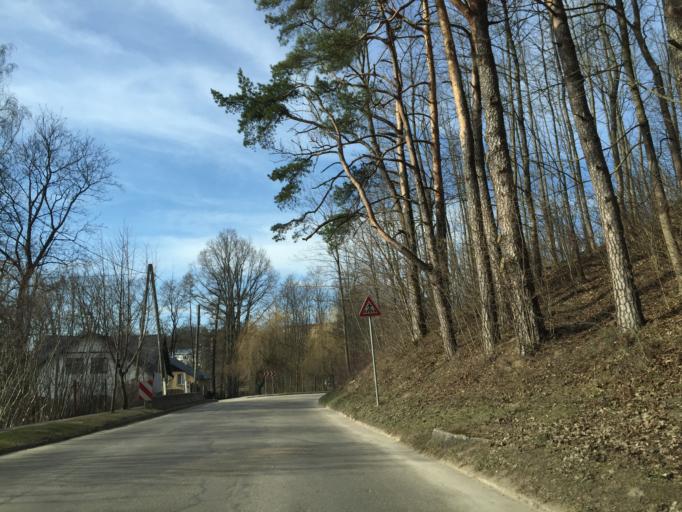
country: LV
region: Ogre
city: Ogre
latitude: 56.8135
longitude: 24.6126
